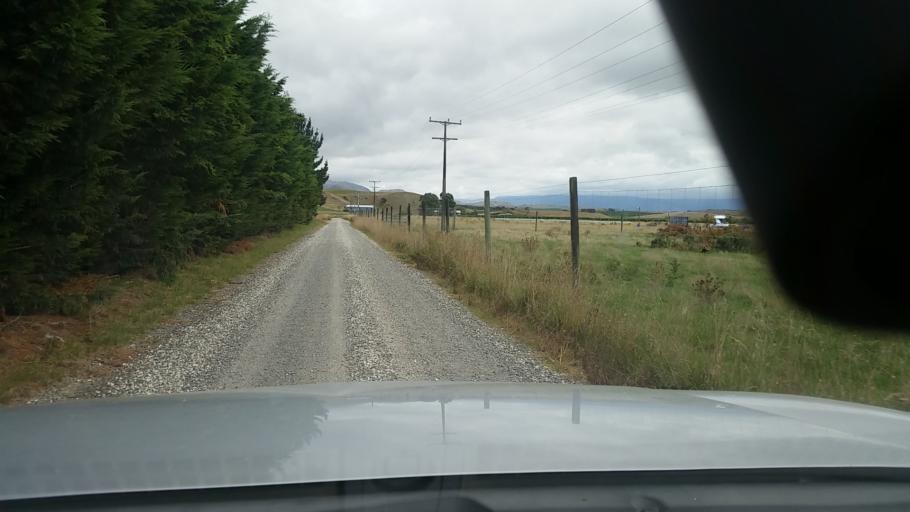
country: NZ
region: Marlborough
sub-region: Marlborough District
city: Blenheim
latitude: -41.6998
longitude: 174.1180
